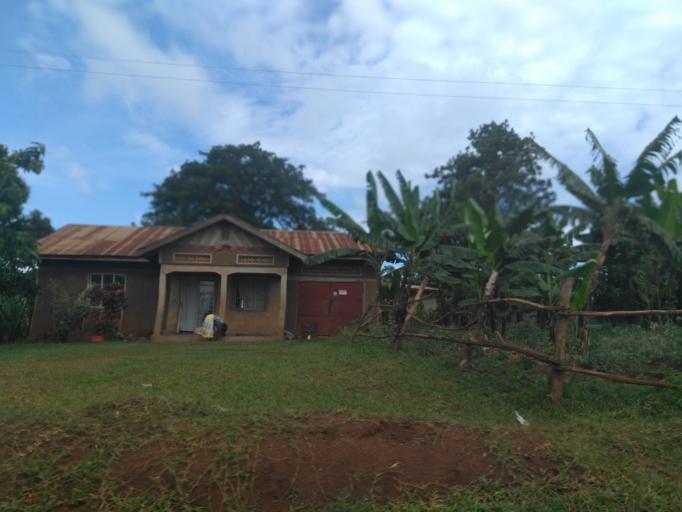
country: UG
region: Central Region
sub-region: Buikwe District
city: Njeru
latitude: 0.4077
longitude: 33.1797
